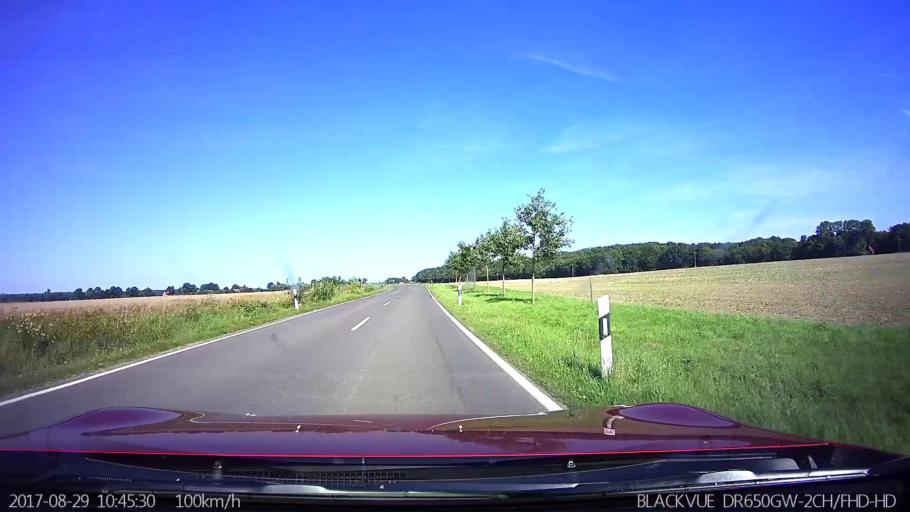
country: DE
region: Mecklenburg-Vorpommern
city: Richtenberg
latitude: 54.2138
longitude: 12.8611
